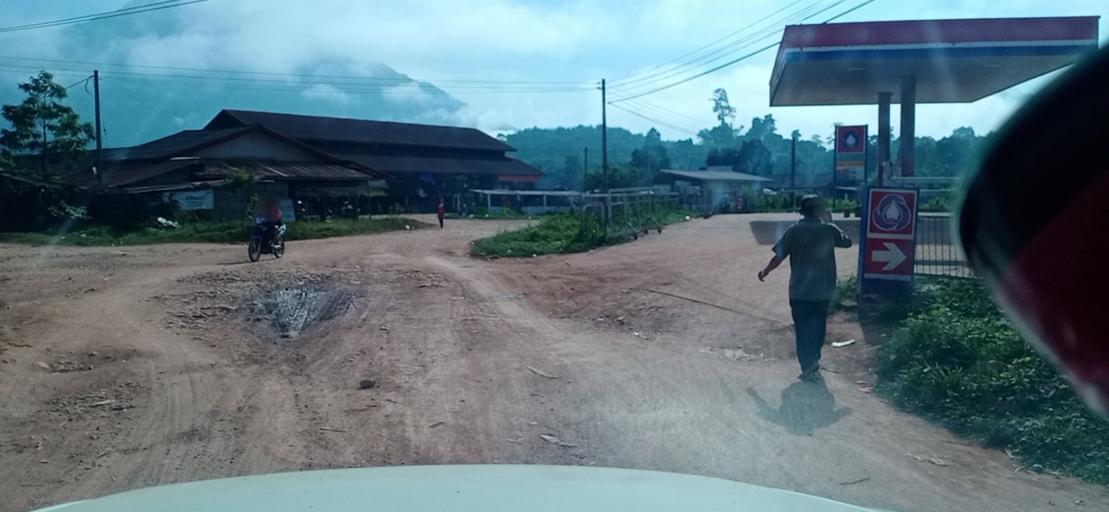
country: TH
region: Changwat Bueng Kan
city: Pak Khat
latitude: 18.6824
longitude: 103.1875
